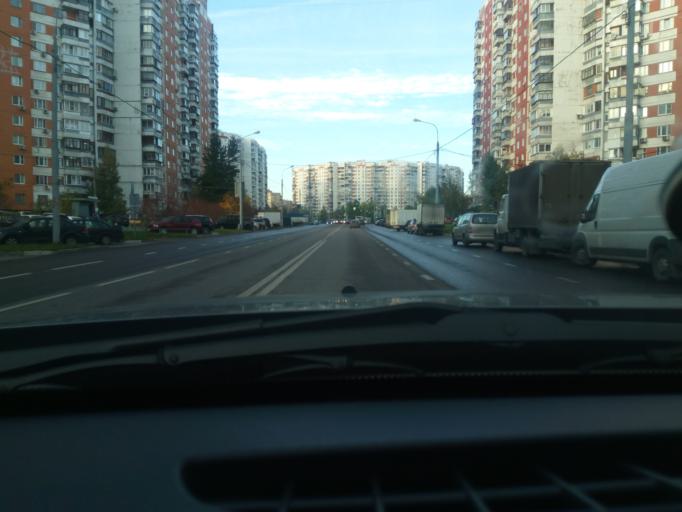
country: RU
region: Moskovskaya
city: Reutov
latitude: 55.7349
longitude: 37.8550
